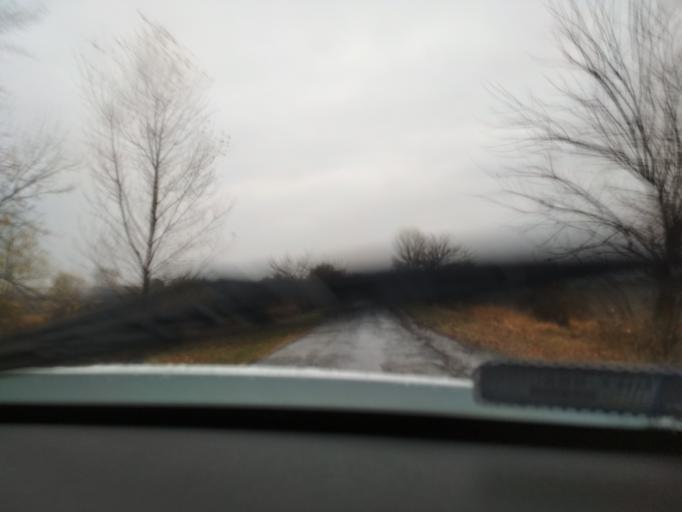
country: HU
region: Csongrad
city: Mindszent
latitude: 46.5376
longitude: 20.1513
